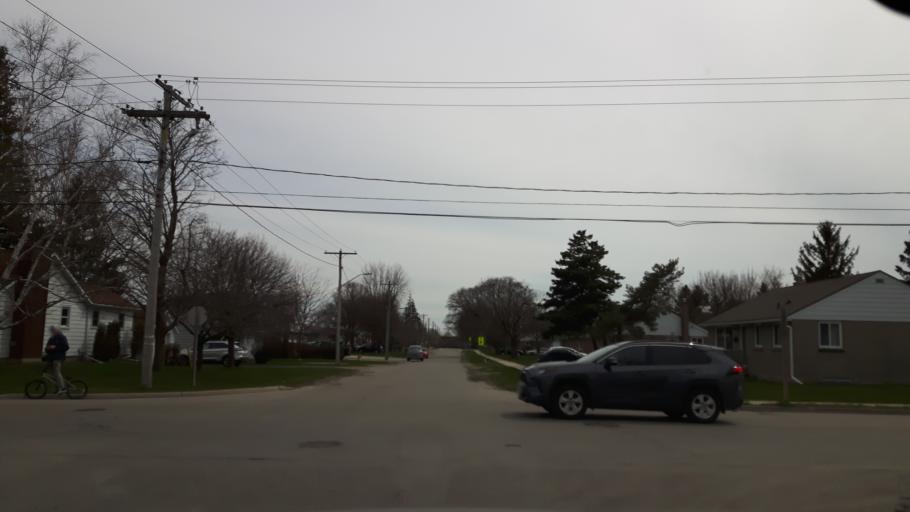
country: CA
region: Ontario
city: Goderich
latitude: 43.7356
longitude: -81.7087
